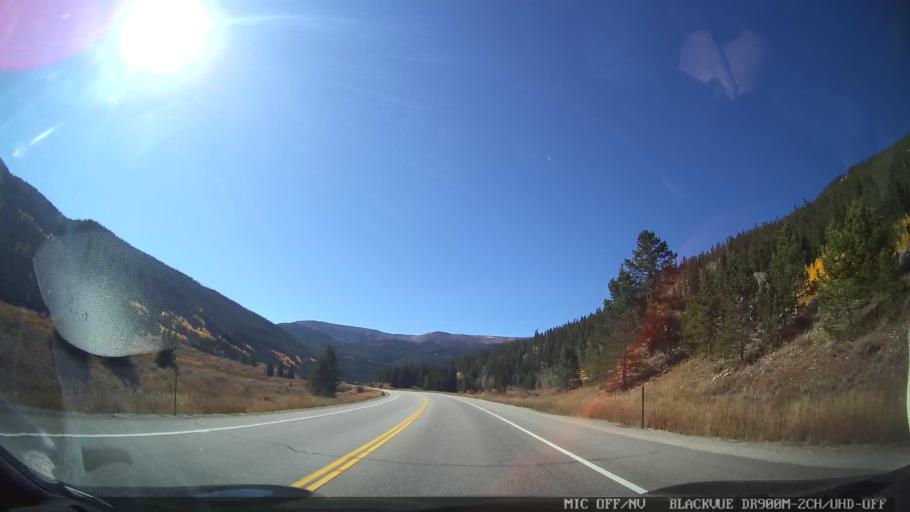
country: US
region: Colorado
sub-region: Lake County
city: Leadville
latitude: 39.3253
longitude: -106.2210
